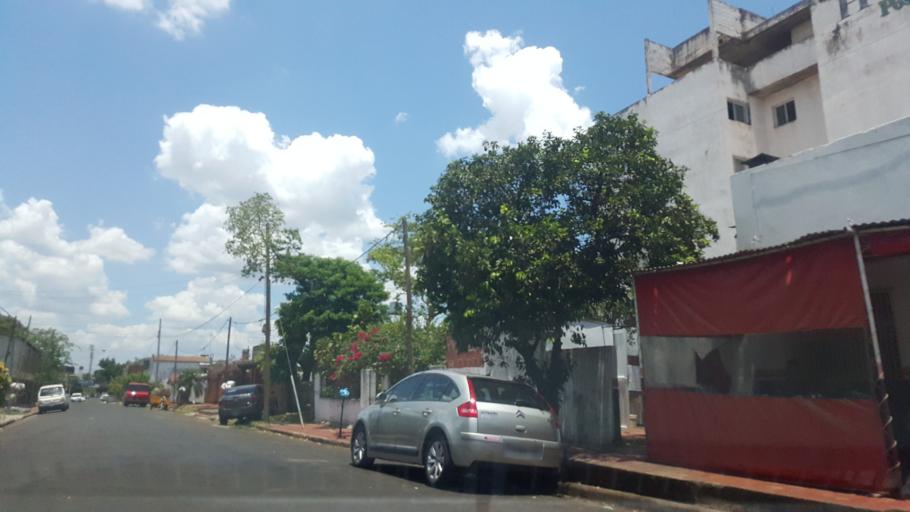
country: AR
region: Misiones
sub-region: Departamento de Capital
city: Posadas
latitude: -27.3855
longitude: -55.9038
